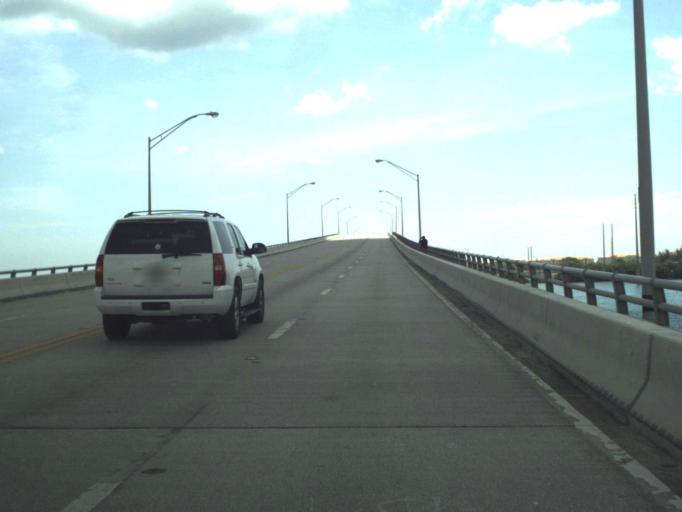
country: US
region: Florida
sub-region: Saint Lucie County
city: Fort Pierce
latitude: 27.4565
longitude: -80.3218
